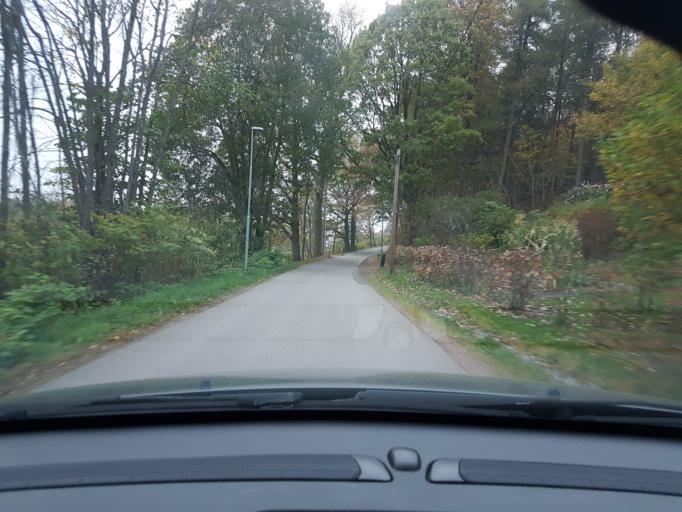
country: SE
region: Vaestra Goetaland
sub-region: Ale Kommun
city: Surte
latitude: 57.8208
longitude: 12.0231
